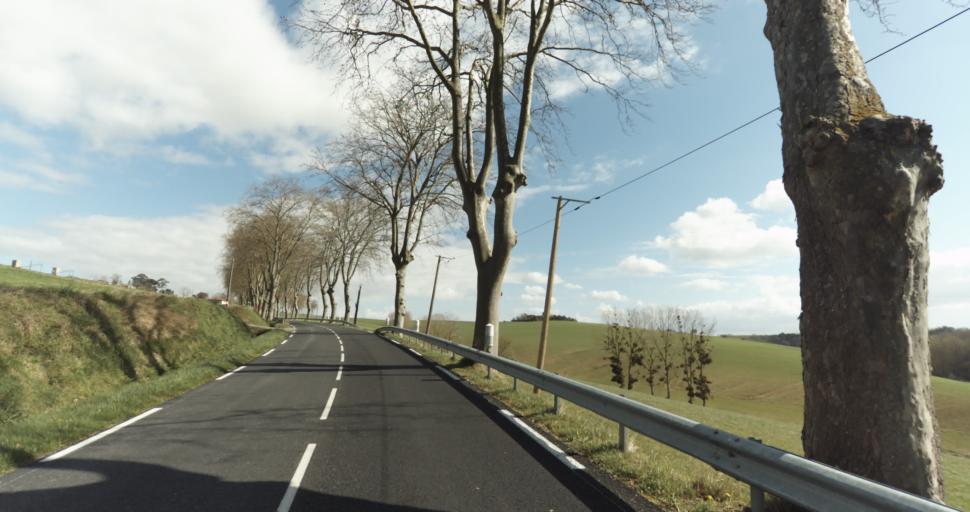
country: FR
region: Midi-Pyrenees
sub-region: Departement de la Haute-Garonne
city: Auterive
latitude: 43.3558
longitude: 1.5106
